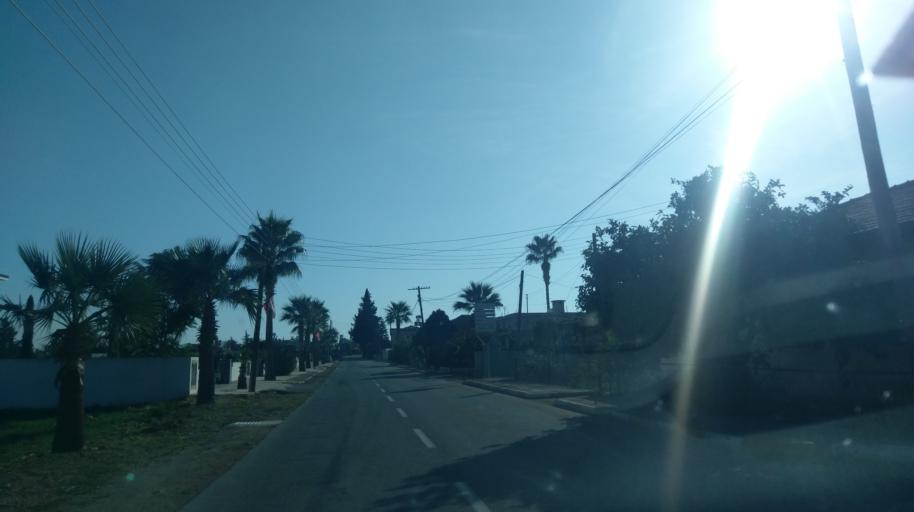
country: CY
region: Larnaka
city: Pergamos
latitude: 35.0489
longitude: 33.7091
